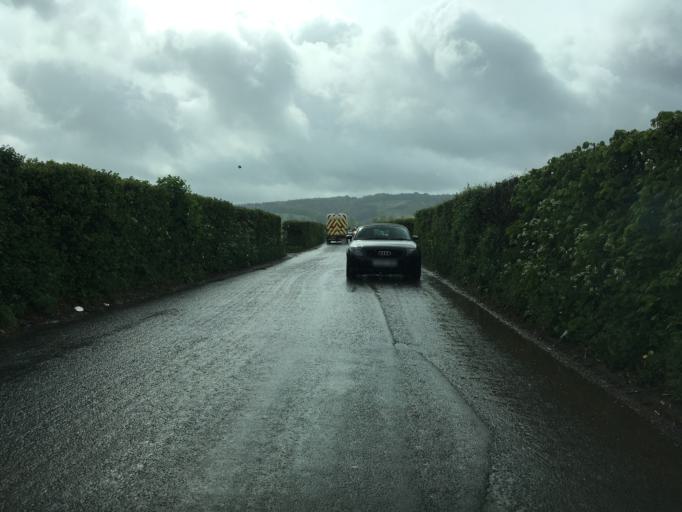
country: GB
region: England
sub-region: North Somerset
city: Burrington
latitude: 51.3432
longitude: -2.7492
